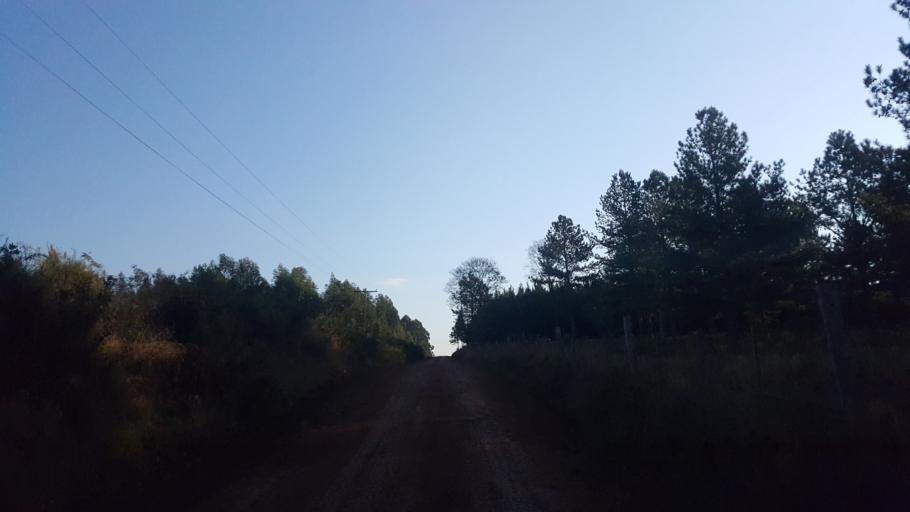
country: AR
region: Misiones
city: Capiovi
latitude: -26.9186
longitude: -55.0517
